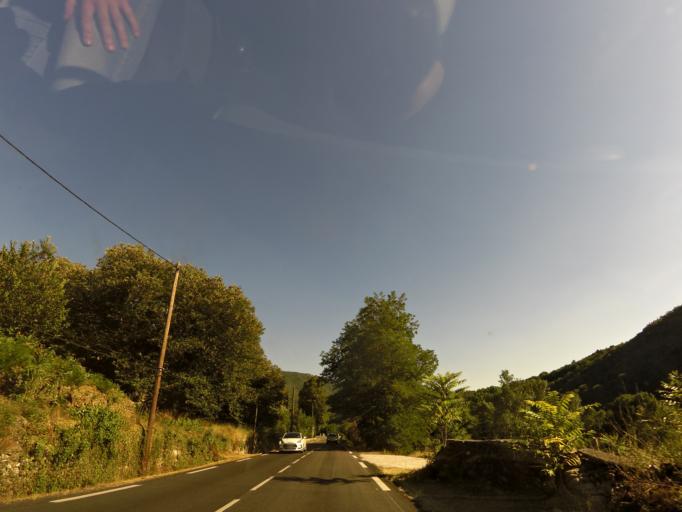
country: FR
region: Languedoc-Roussillon
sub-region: Departement du Gard
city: Sumene
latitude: 43.9752
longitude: 3.6864
